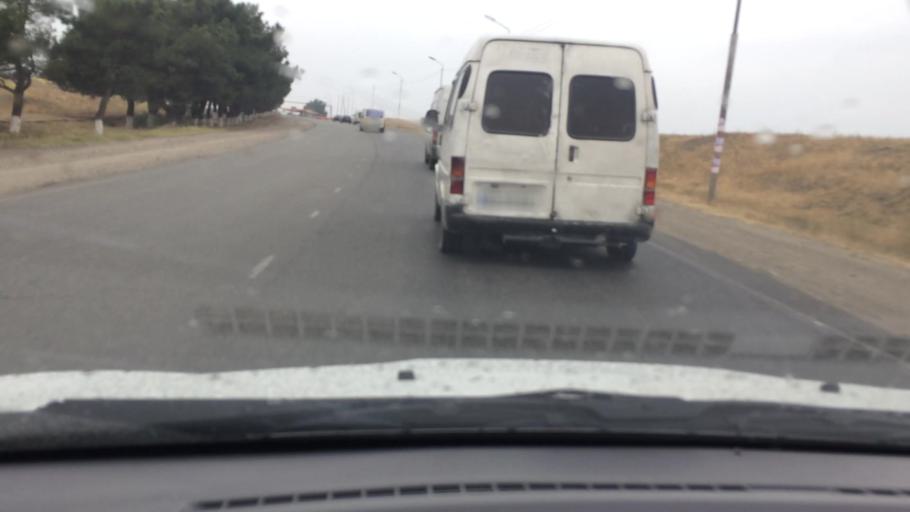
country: GE
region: Kvemo Kartli
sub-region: Marneuli
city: Marneuli
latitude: 41.5035
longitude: 44.8011
